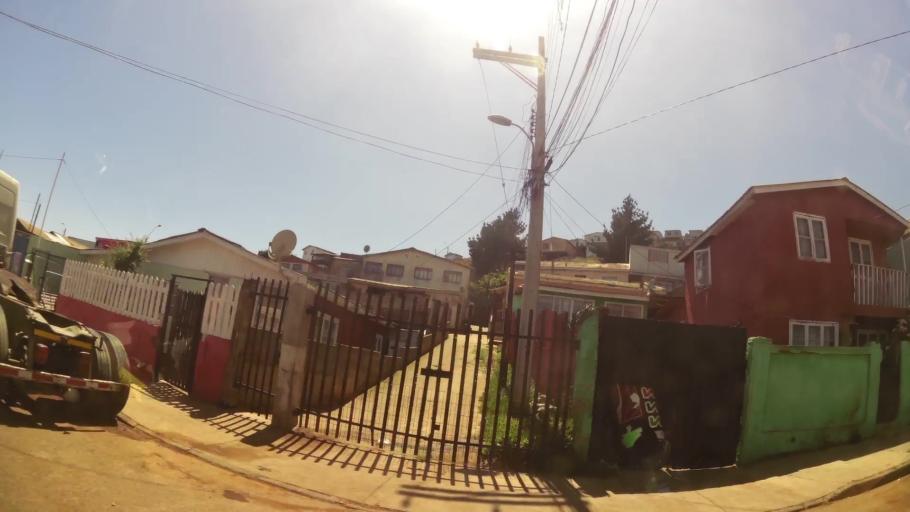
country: CL
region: Valparaiso
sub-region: Provincia de Valparaiso
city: Valparaiso
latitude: -33.0366
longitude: -71.6511
